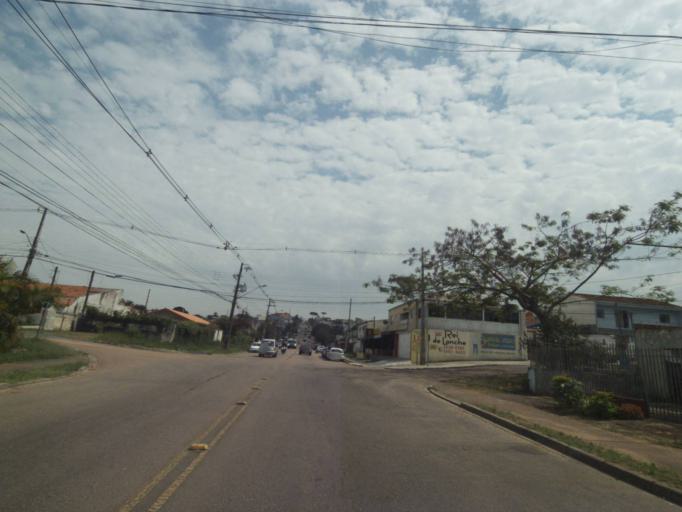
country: BR
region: Parana
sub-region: Pinhais
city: Pinhais
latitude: -25.4071
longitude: -49.2037
